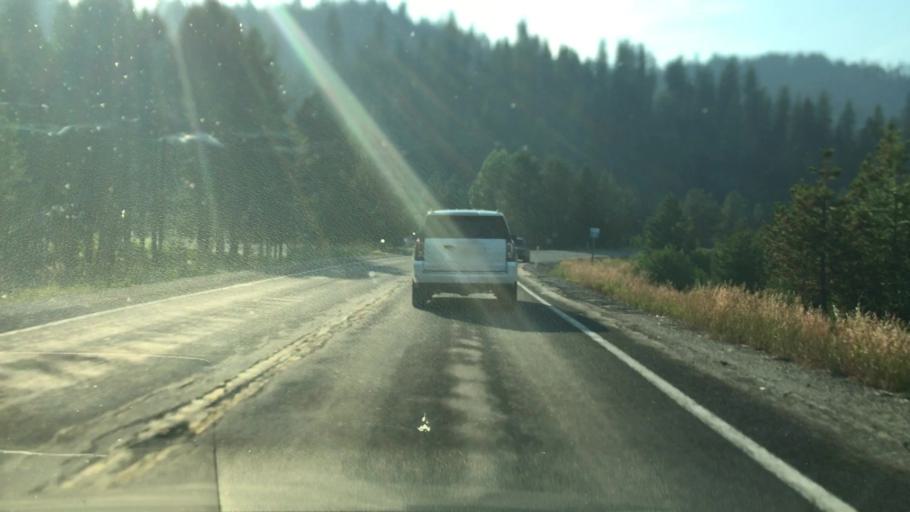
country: US
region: Idaho
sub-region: Valley County
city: Cascade
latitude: 44.2973
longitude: -116.0870
